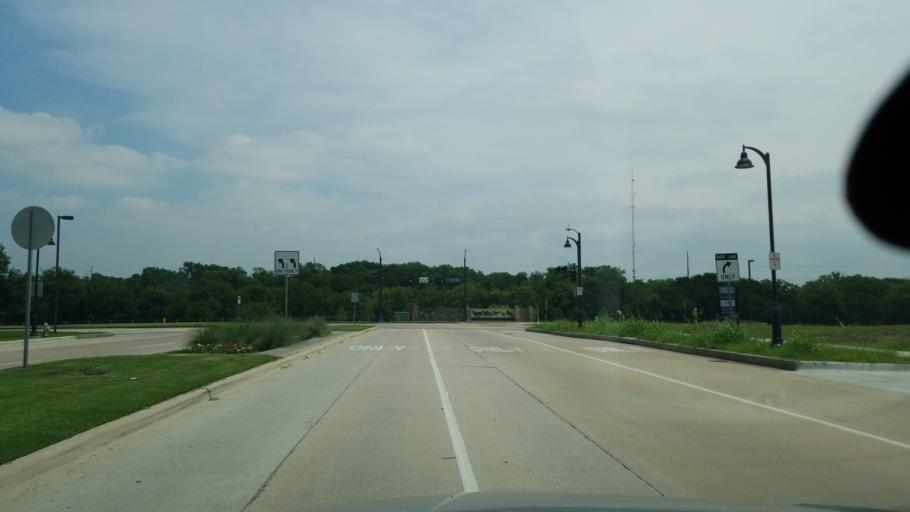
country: US
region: Texas
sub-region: Dallas County
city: Irving
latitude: 32.8707
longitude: -96.9338
